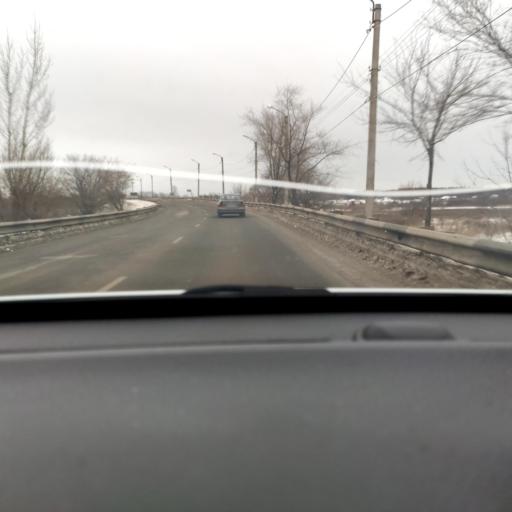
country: RU
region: Voronezj
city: Somovo
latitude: 51.7433
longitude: 39.3412
